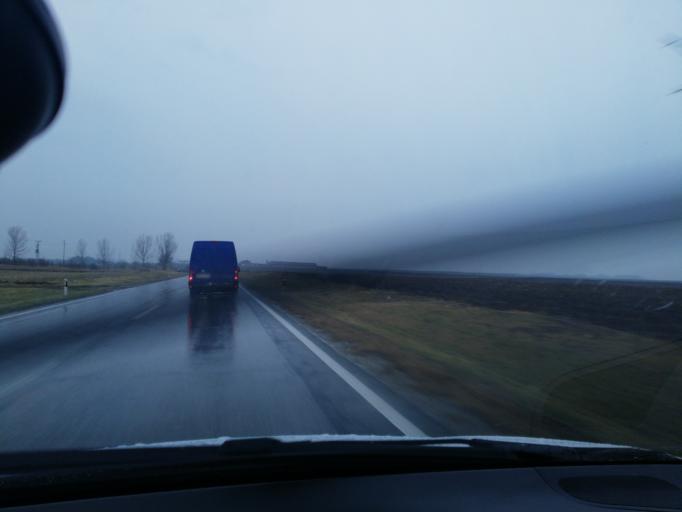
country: RS
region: Autonomna Pokrajina Vojvodina
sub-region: Sremski Okrug
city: Ruma
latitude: 45.0460
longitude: 19.8414
